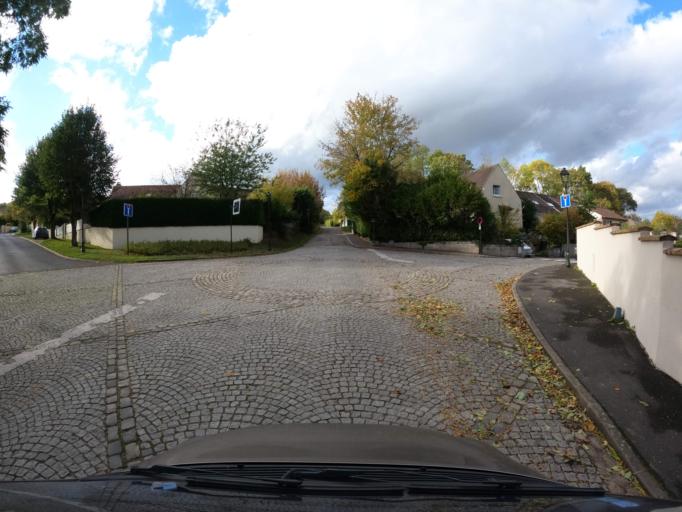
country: FR
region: Ile-de-France
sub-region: Departement de Seine-et-Marne
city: Coupvray
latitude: 48.8905
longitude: 2.7901
